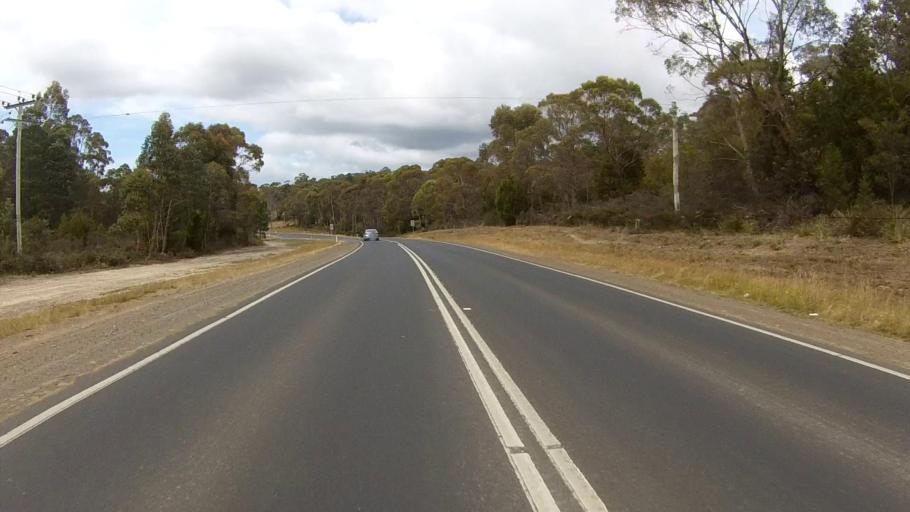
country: AU
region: Tasmania
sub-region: Kingborough
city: Margate
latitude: -43.0484
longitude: 147.2632
